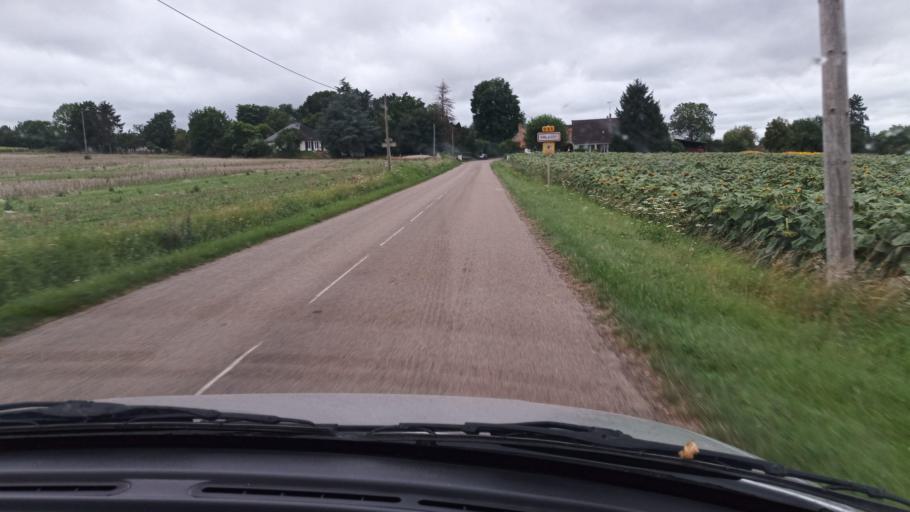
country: FR
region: Bourgogne
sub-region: Departement de l'Yonne
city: Cheroy
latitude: 48.2370
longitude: 3.0524
